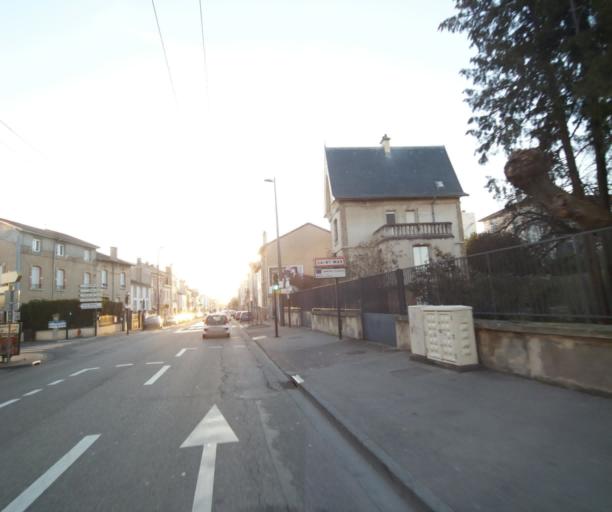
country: FR
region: Lorraine
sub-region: Departement de Meurthe-et-Moselle
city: Saint-Max
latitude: 48.7029
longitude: 6.2160
